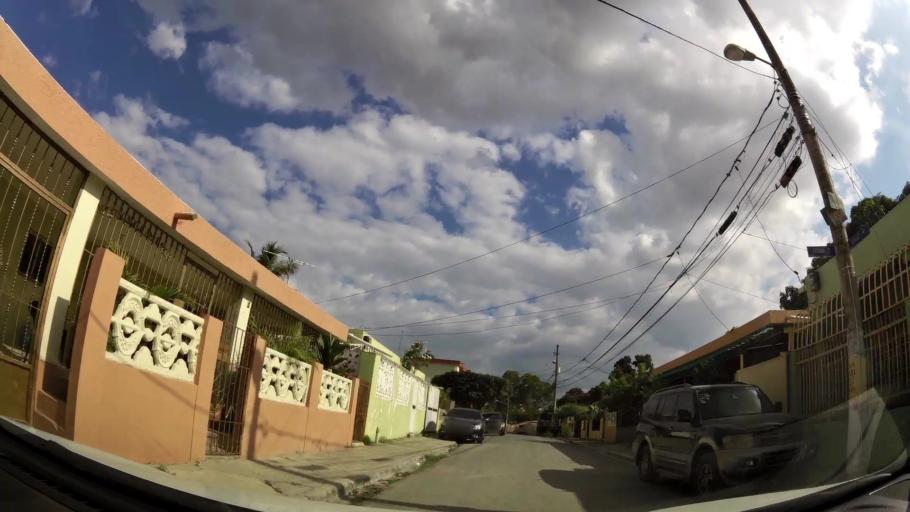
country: DO
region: Nacional
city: Ensanche Luperon
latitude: 18.5548
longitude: -69.9016
